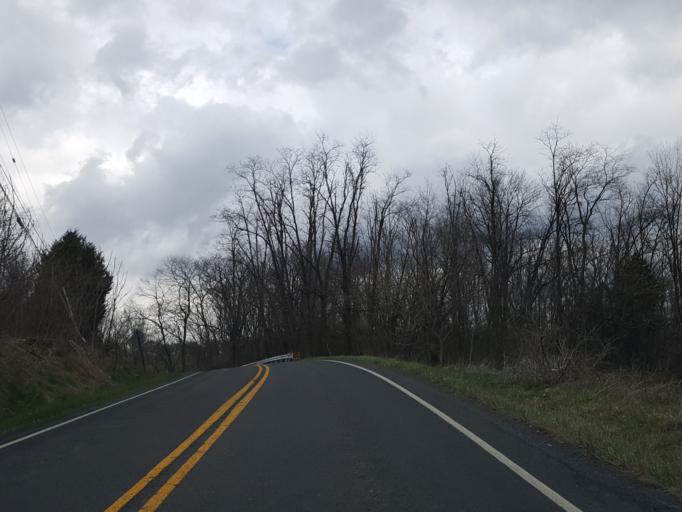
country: US
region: Pennsylvania
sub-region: Berks County
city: Robesonia
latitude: 40.4110
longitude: -76.1149
